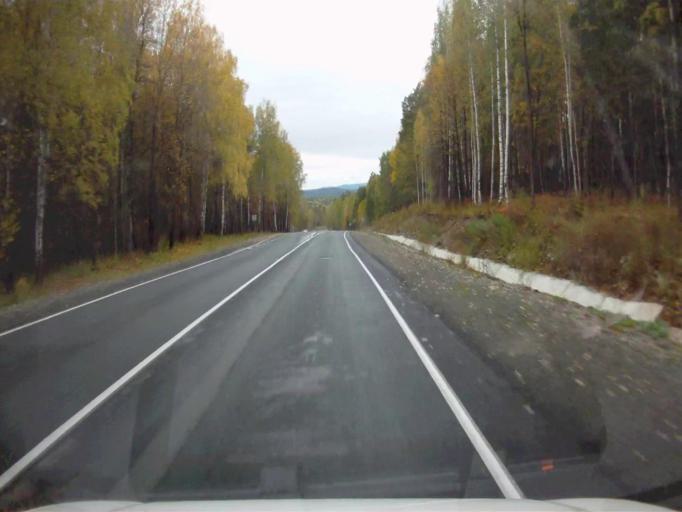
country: RU
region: Chelyabinsk
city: Nyazepetrovsk
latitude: 56.0520
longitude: 59.7427
